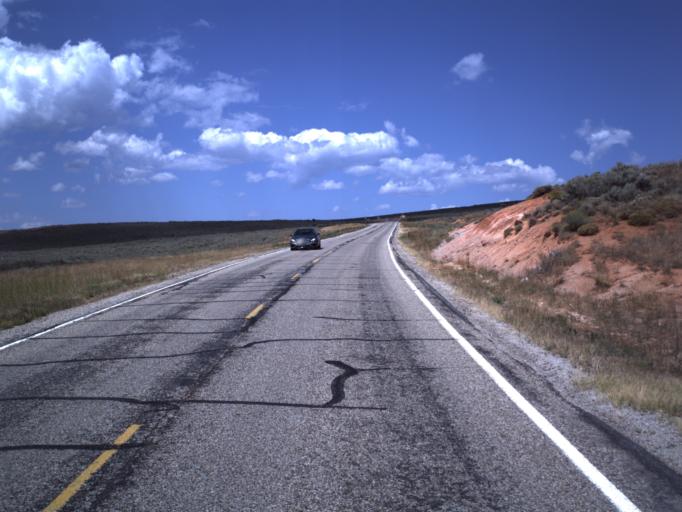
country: US
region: Utah
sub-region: Rich County
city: Randolph
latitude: 41.8019
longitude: -111.2446
